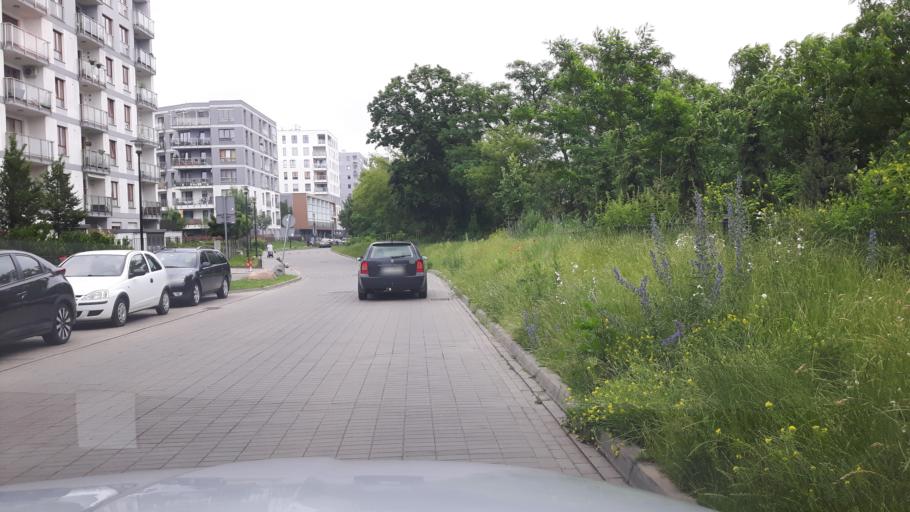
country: PL
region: Masovian Voivodeship
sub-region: Warszawa
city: Zoliborz
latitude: 52.2567
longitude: 20.9730
